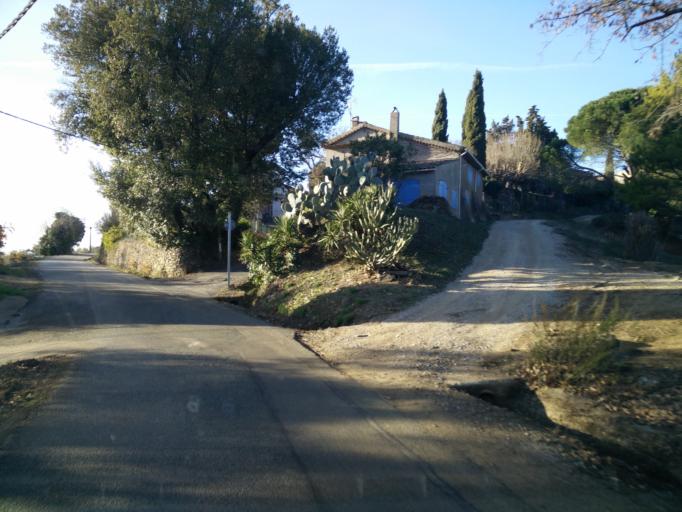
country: FR
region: Provence-Alpes-Cote d'Azur
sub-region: Departement du Var
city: La Garde-Freinet
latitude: 43.3422
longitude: 6.4927
